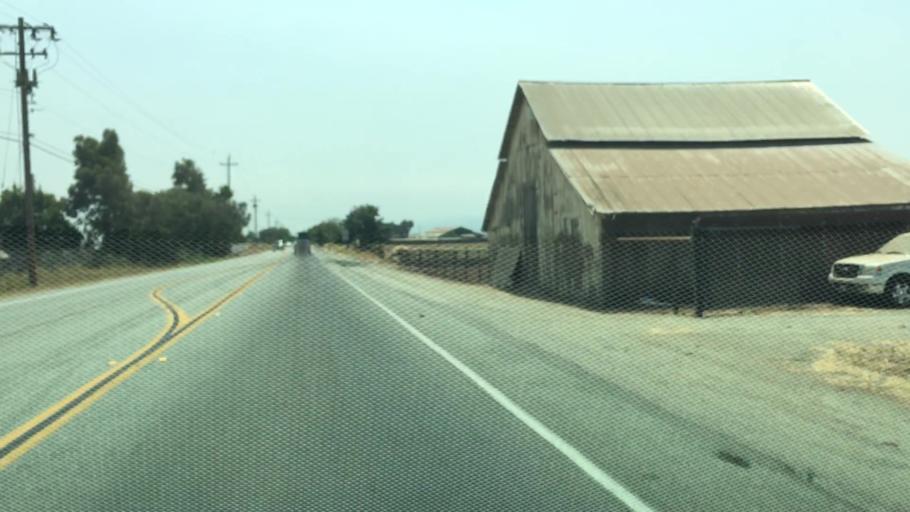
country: US
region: California
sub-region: Santa Clara County
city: Gilroy
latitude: 37.0270
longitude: -121.5271
